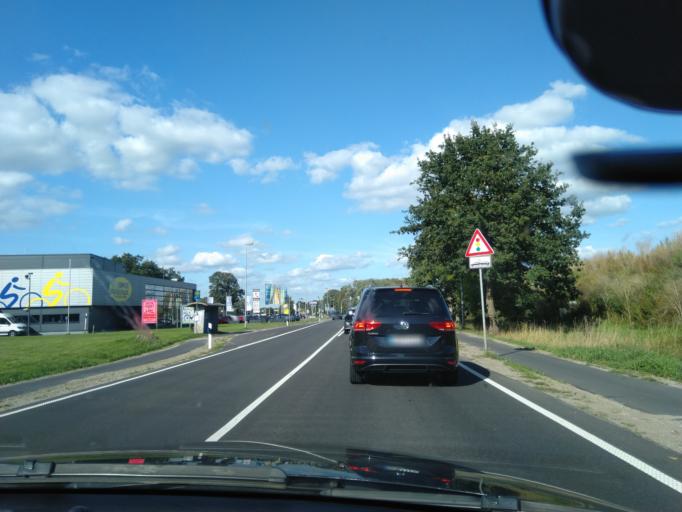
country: DE
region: Lower Saxony
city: Leer
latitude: 53.2575
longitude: 7.4589
